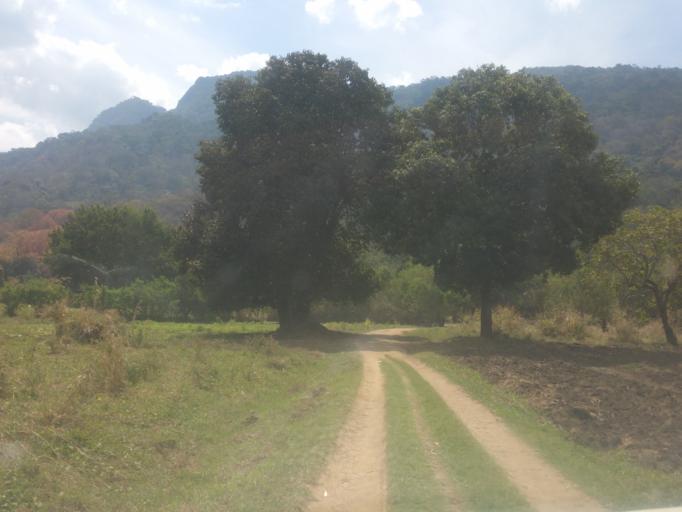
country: TZ
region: Morogoro
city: Kidatu
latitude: -7.8353
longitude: 36.8912
